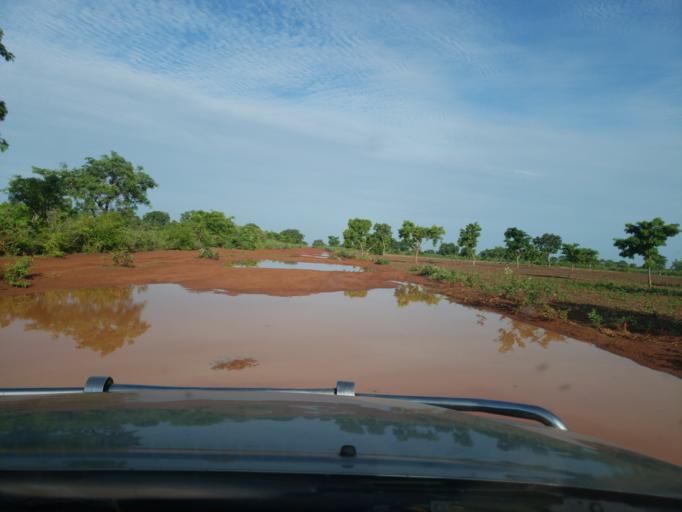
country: ML
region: Sikasso
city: Koutiala
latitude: 12.4279
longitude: -5.6290
